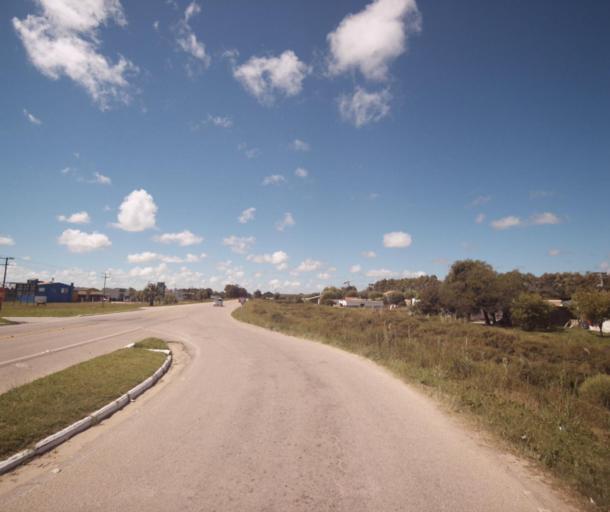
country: BR
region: Rio Grande do Sul
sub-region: Santa Vitoria Do Palmar
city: Santa Vitoria do Palmar
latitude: -33.5309
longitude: -53.3453
